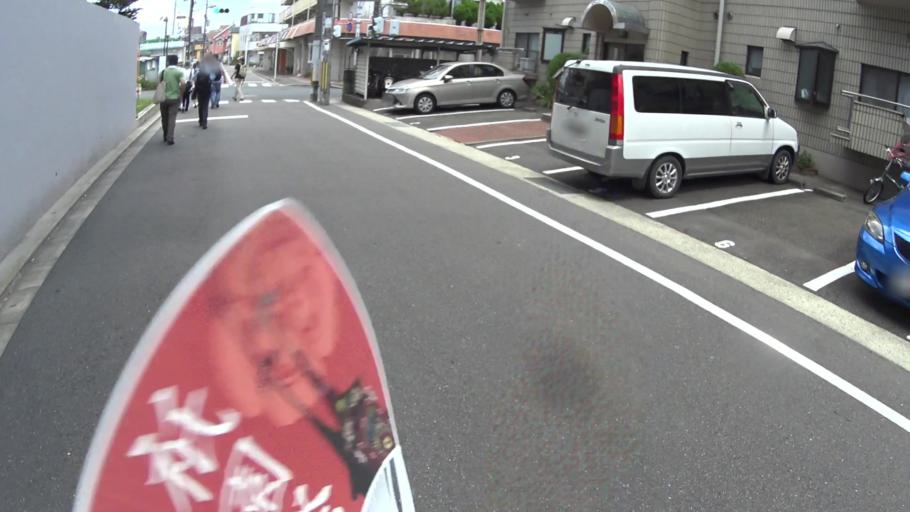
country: JP
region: Kyoto
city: Yawata
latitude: 34.9108
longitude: 135.6977
